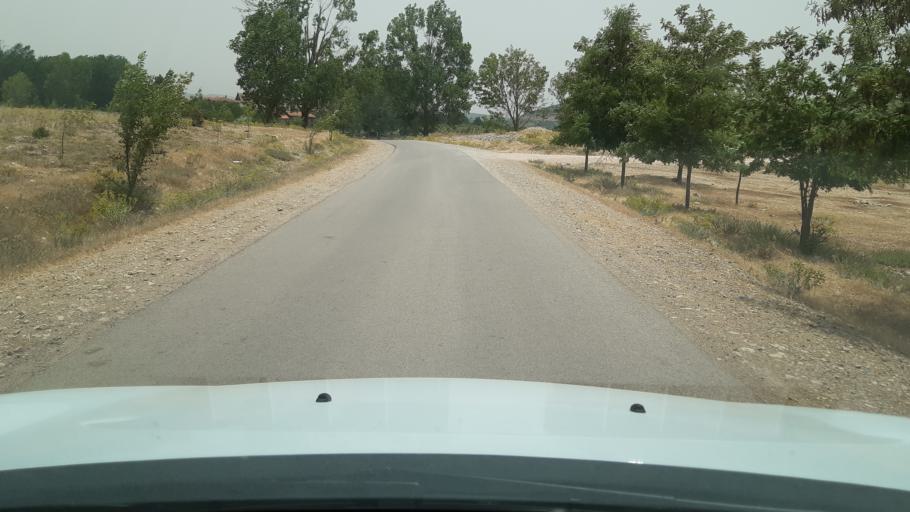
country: MA
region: Meknes-Tafilalet
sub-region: Ifrane
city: Ifrane
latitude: 33.6470
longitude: -5.0208
